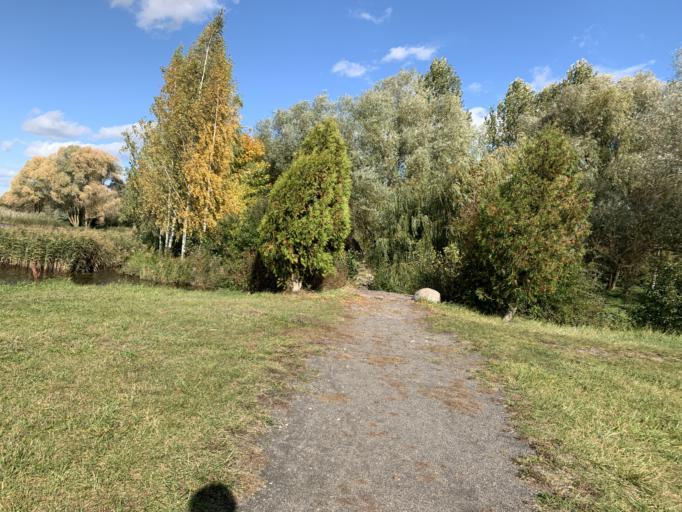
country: BY
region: Minsk
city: Nyasvizh
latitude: 53.2269
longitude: 26.7028
